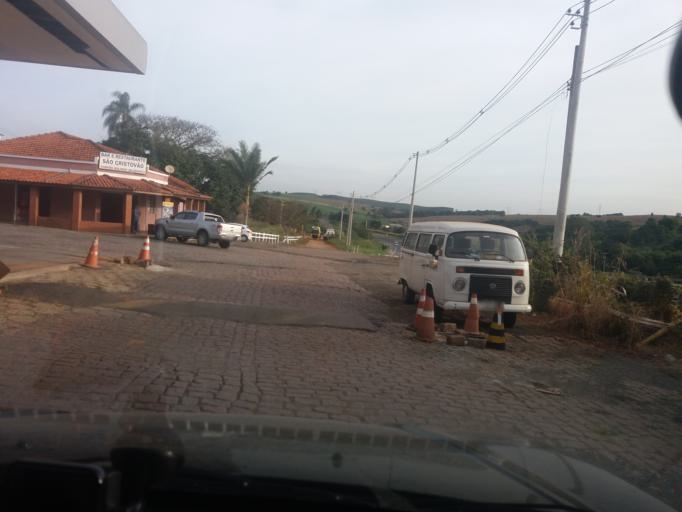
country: BR
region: Sao Paulo
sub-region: Itapetininga
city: Itapetininga
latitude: -23.7694
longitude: -48.1332
